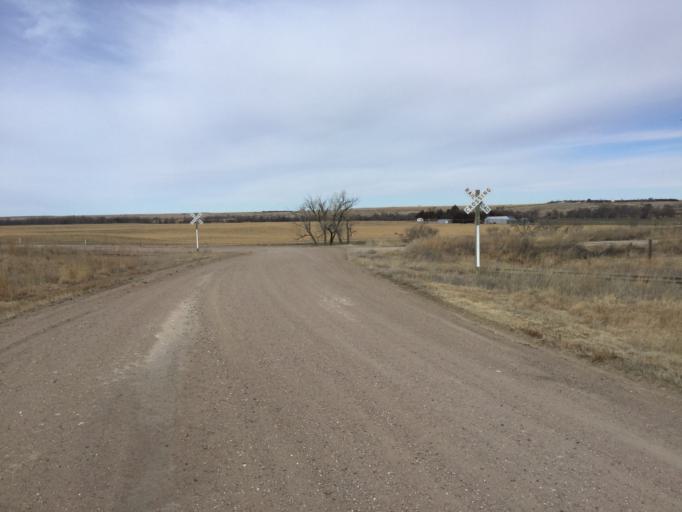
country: US
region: Kansas
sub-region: Rawlins County
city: Atwood
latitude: 39.8575
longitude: -100.9241
